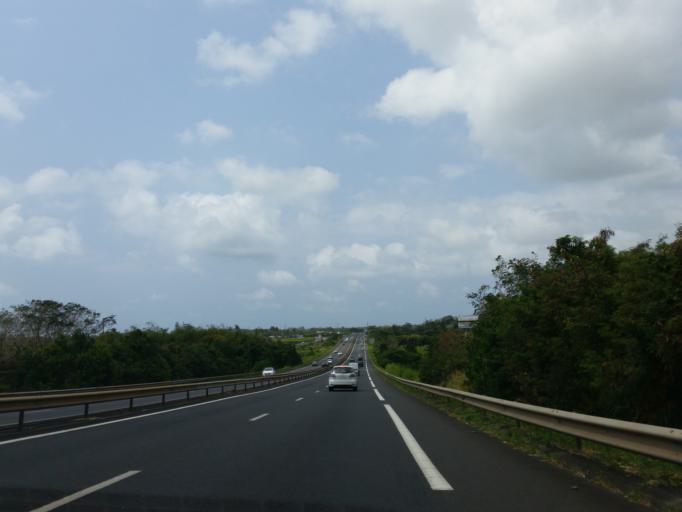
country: RE
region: Reunion
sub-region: Reunion
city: Sainte-Suzanne
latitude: -20.9138
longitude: 55.6085
